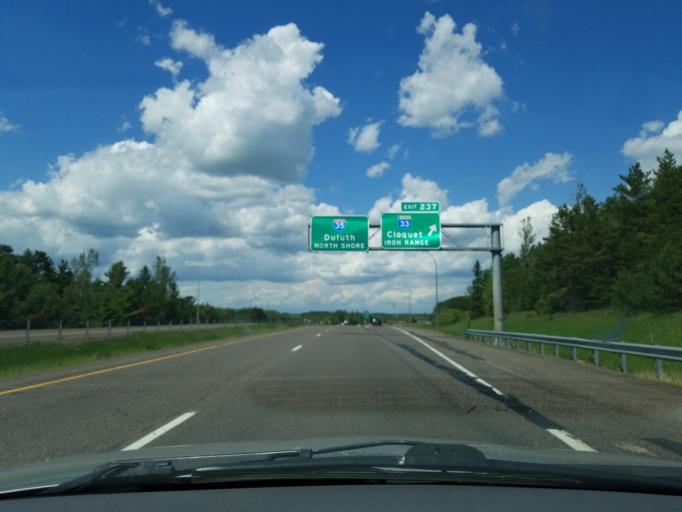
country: US
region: Minnesota
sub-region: Carlton County
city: Cloquet
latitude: 46.6842
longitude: -92.4599
